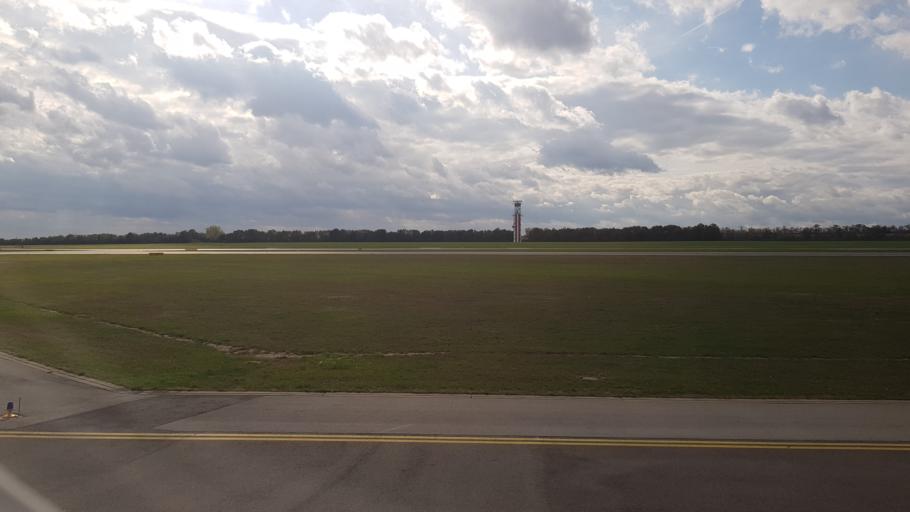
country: AT
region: Lower Austria
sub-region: Politischer Bezirk Bruck an der Leitha
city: Enzersdorf an der Fischa
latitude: 48.1038
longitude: 16.5845
